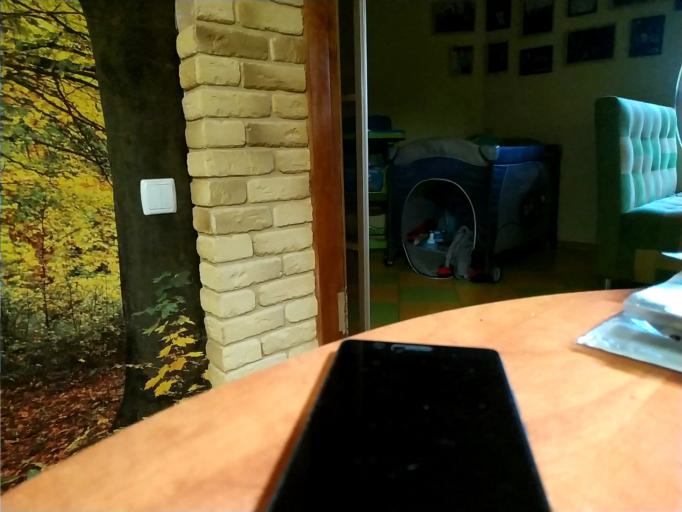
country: RU
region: Orjol
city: Znamenskoye
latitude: 53.4680
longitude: 35.5195
